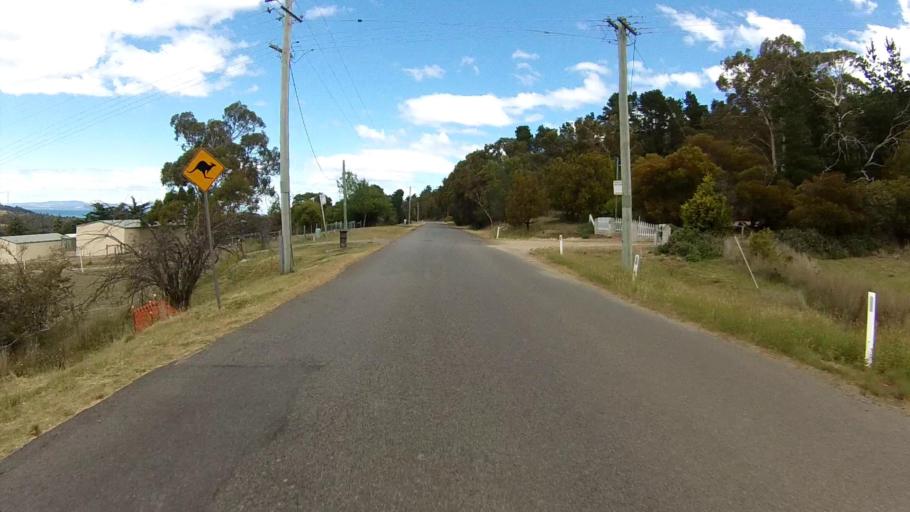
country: AU
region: Tasmania
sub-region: Clarence
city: Acton Park
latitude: -42.8652
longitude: 147.4698
